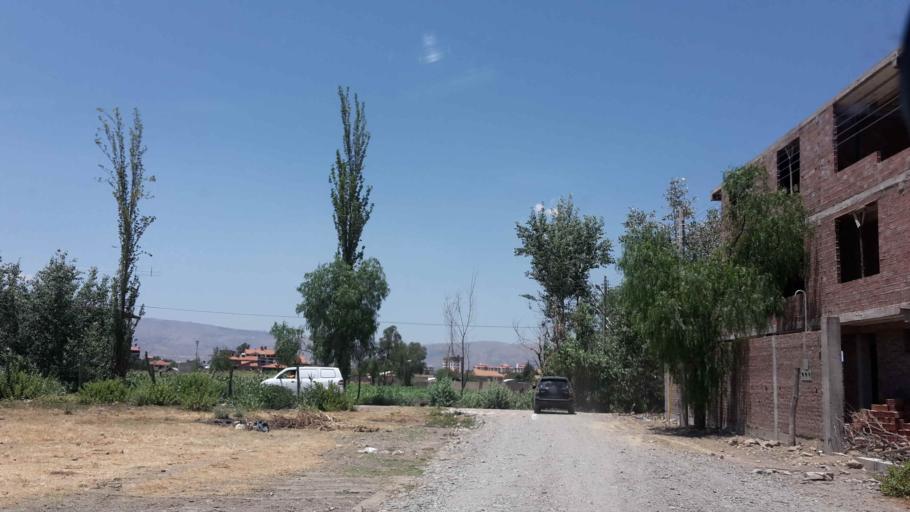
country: BO
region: Cochabamba
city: Cochabamba
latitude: -17.3711
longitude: -66.1951
